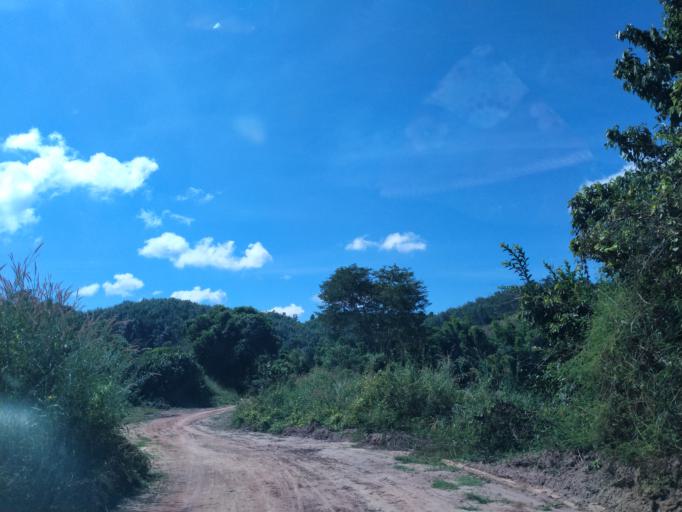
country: LA
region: Vientiane
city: Muang Phon-Hong
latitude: 18.6191
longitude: 102.8558
